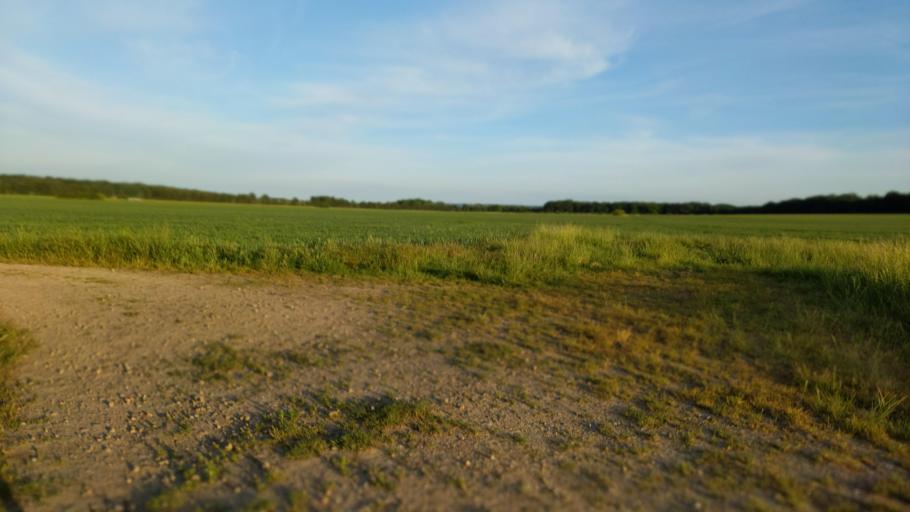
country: DE
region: Lower Saxony
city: Sickte
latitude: 52.2325
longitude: 10.5873
